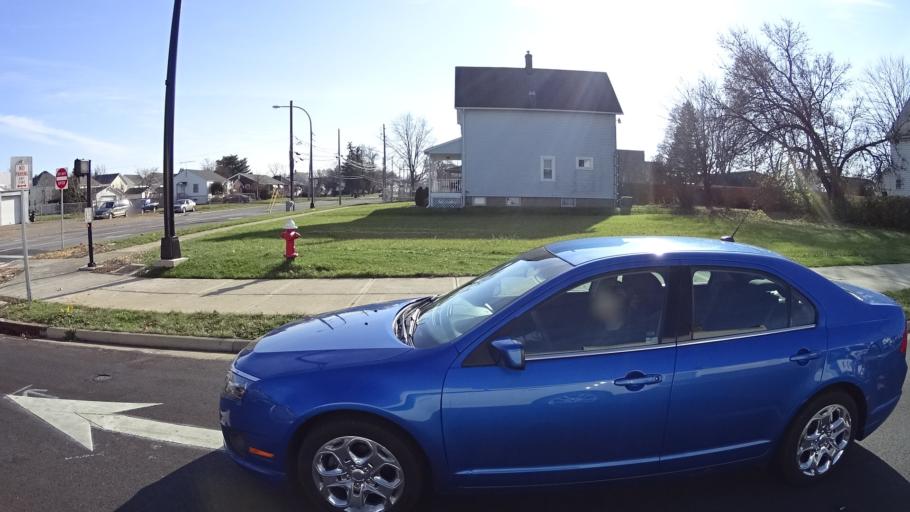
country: US
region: Ohio
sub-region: Lorain County
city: Elyria
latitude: 41.3649
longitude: -82.1164
